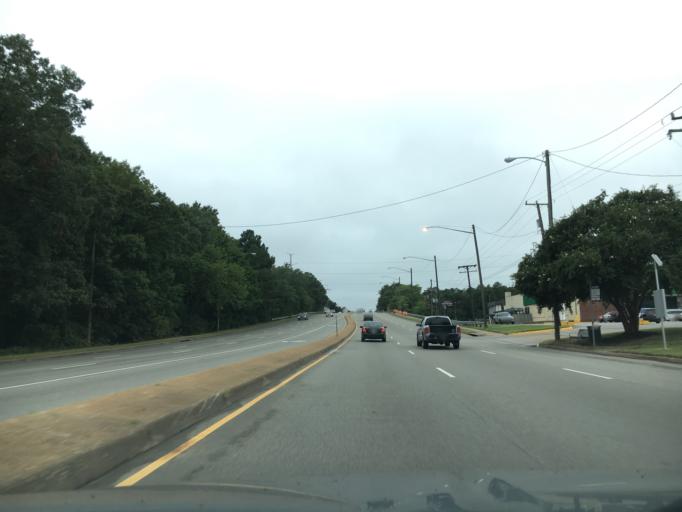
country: US
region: Virginia
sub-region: City of Richmond
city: Richmond
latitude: 37.5009
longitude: -77.4757
